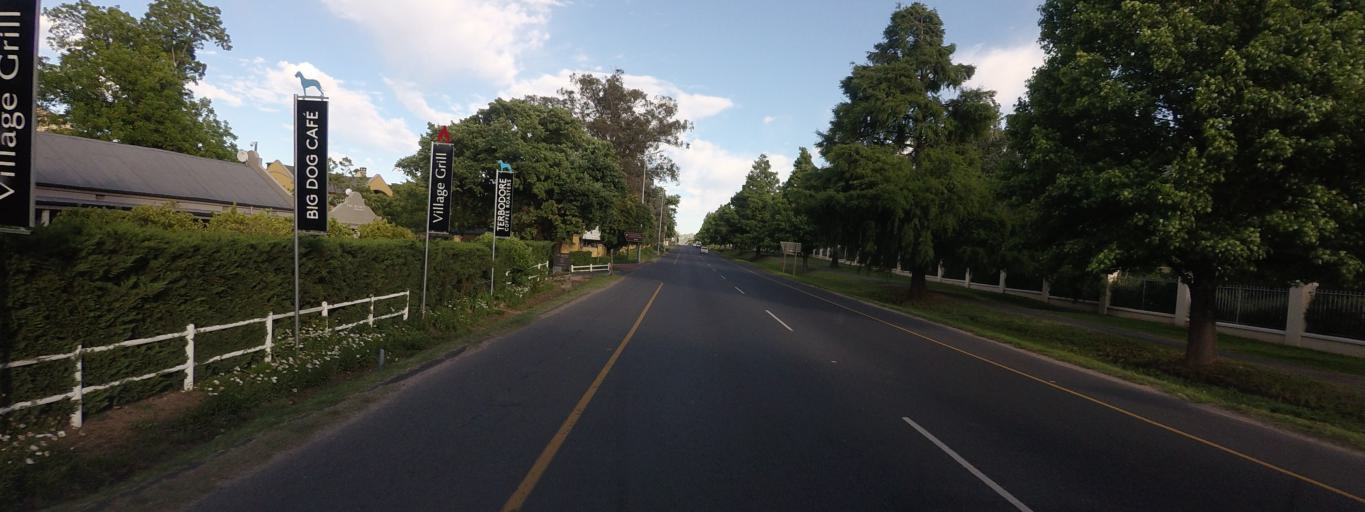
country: ZA
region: Western Cape
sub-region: Cape Winelands District Municipality
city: Paarl
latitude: -33.9003
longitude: 19.1058
